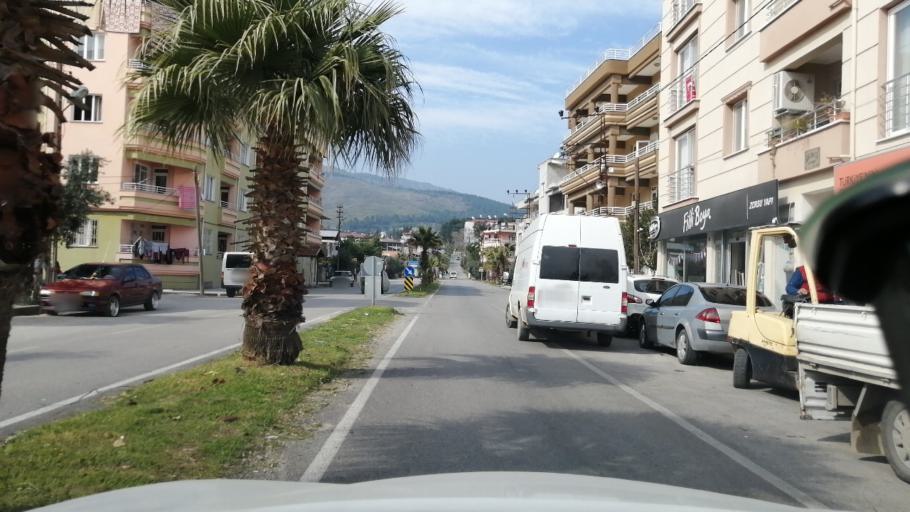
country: TR
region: Hatay
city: Serinyol
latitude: 36.3522
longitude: 36.2115
